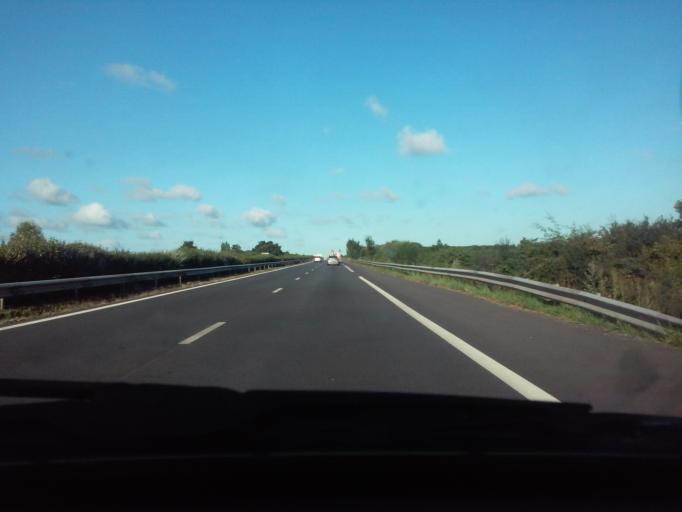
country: FR
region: Pays de la Loire
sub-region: Departement de la Loire-Atlantique
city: Saint-Nazaire
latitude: 47.2930
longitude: -2.2267
